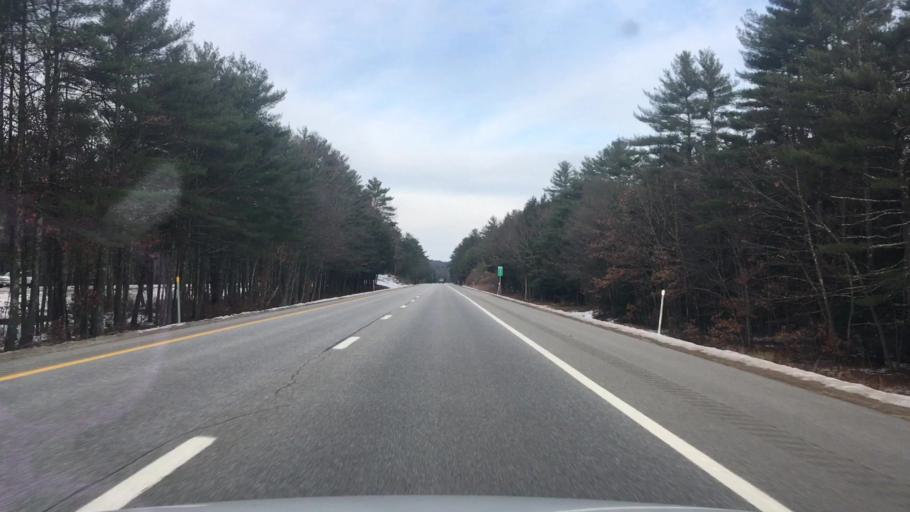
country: US
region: New Hampshire
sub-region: Merrimack County
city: Contoocook
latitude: 43.2269
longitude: -71.7333
